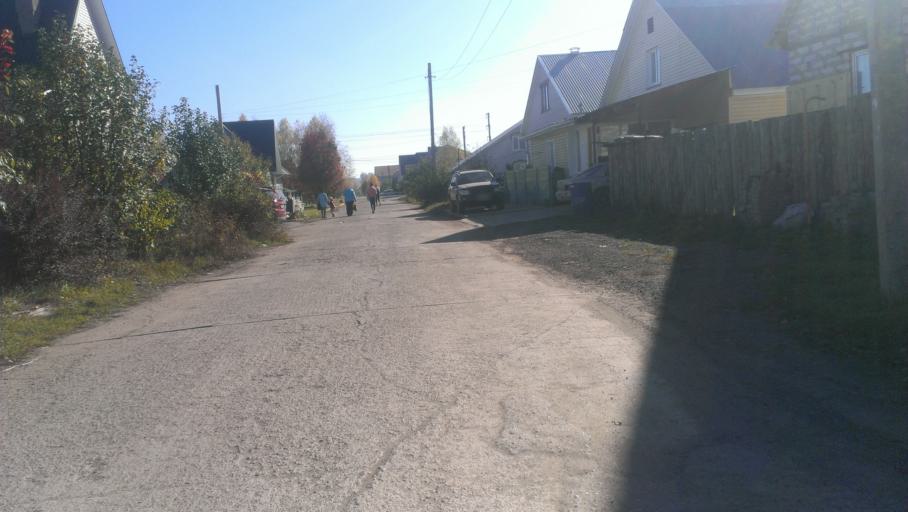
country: RU
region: Altai Krai
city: Novosilikatnyy
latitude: 53.3540
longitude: 83.6321
